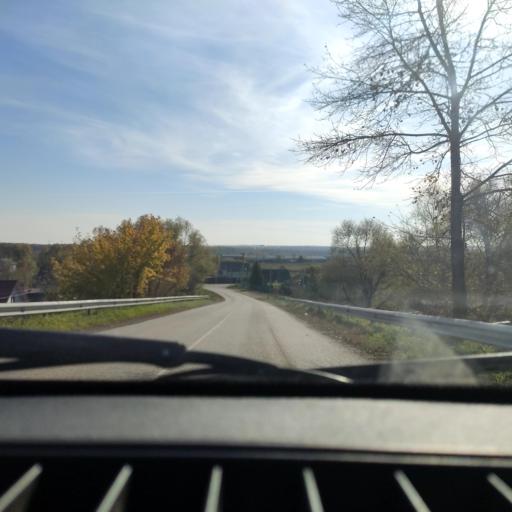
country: RU
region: Bashkortostan
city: Avdon
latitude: 54.6512
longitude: 55.7779
